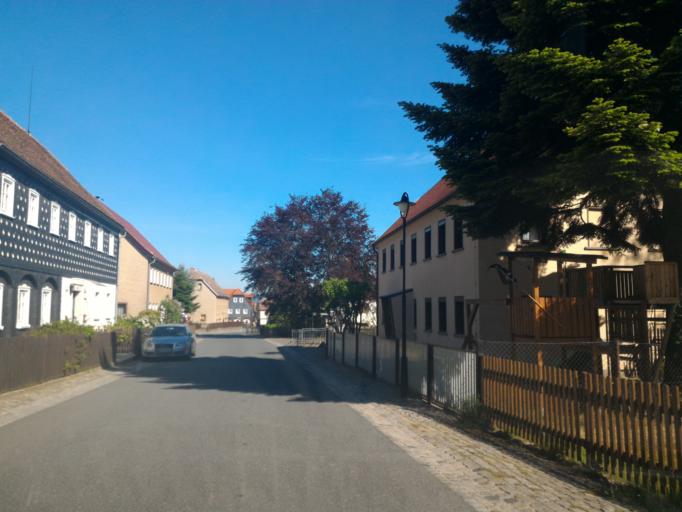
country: DE
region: Saxony
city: Niedercunnersdorf
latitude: 51.0260
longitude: 14.6758
